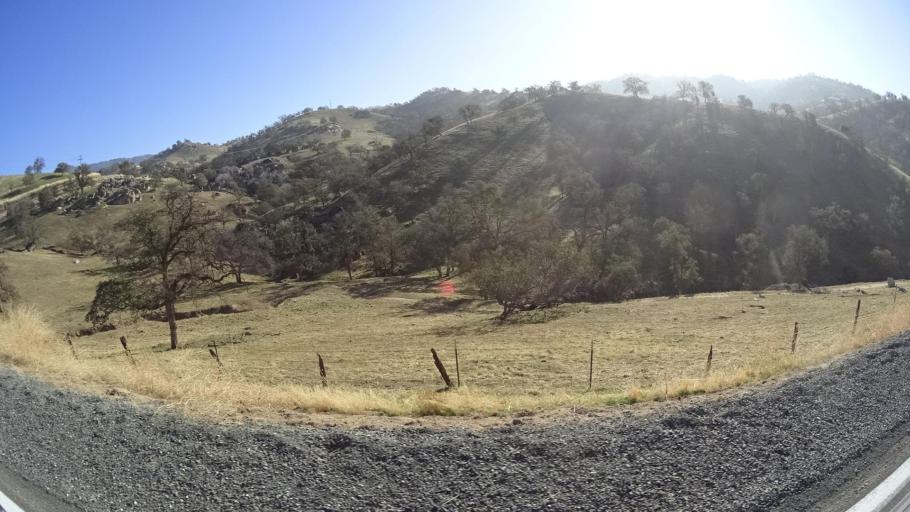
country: US
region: California
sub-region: Kern County
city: Alta Sierra
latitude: 35.7163
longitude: -118.8115
